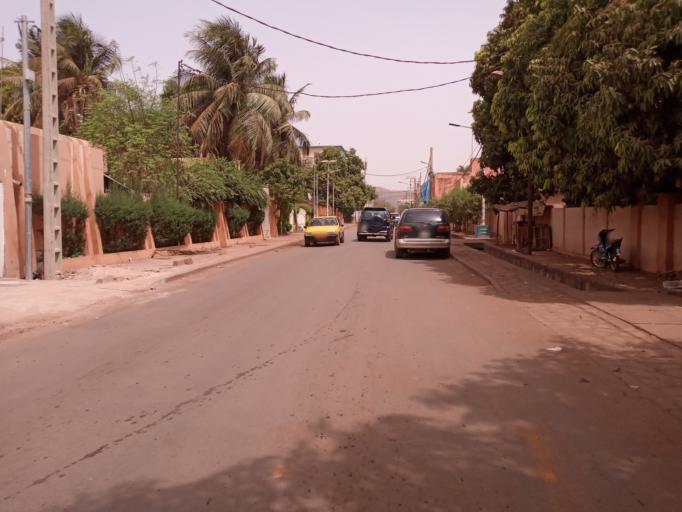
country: ML
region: Bamako
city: Bamako
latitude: 12.6444
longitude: -7.9799
